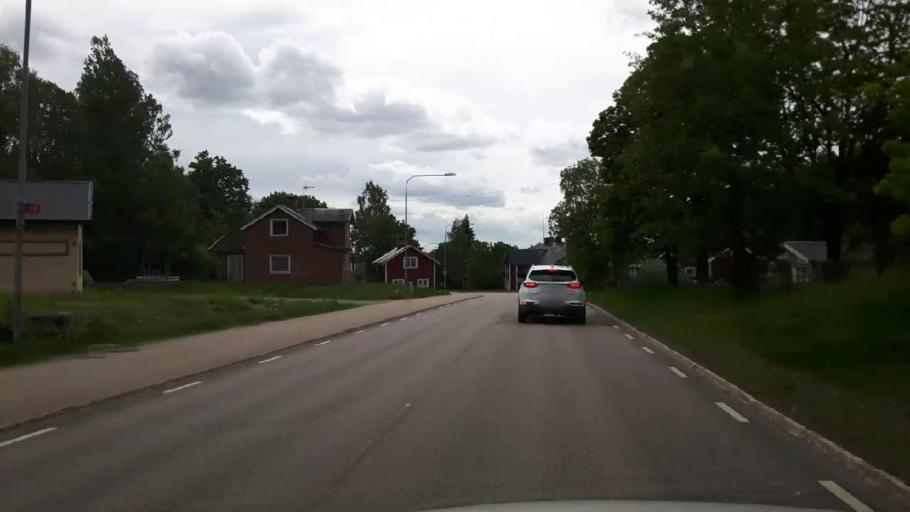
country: SE
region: Vaestmanland
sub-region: Norbergs Kommun
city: Norberg
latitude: 60.0781
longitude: 15.9316
